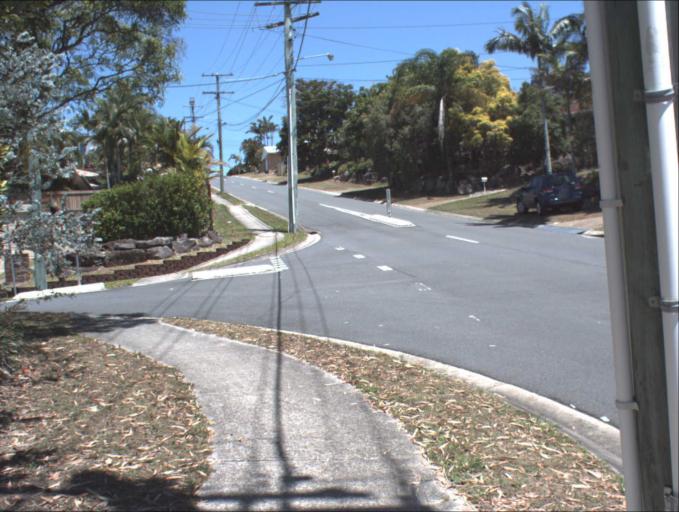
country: AU
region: Queensland
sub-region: Logan
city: Springwood
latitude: -27.6041
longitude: 153.1320
